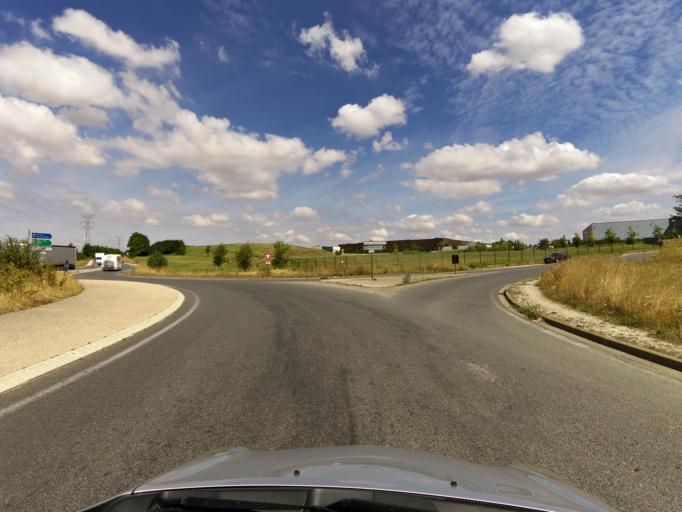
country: FR
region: Ile-de-France
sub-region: Departement de Seine-et-Marne
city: Chauconin-Neufmontiers
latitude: 48.9634
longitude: 2.8614
